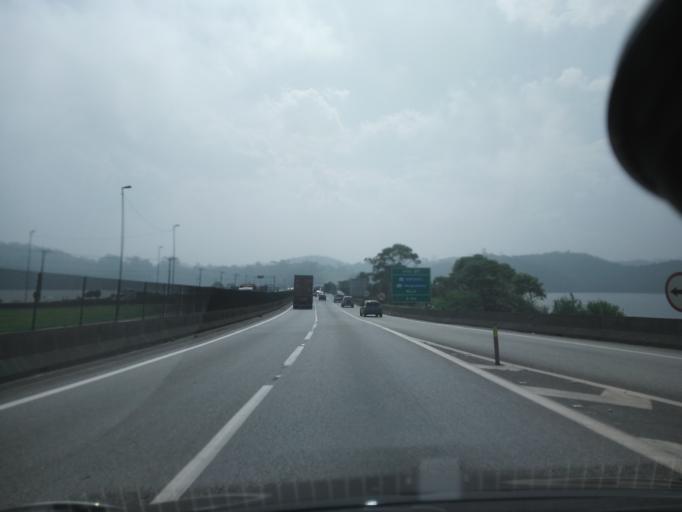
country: BR
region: Sao Paulo
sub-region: Sao Bernardo Do Campo
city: Sao Bernardo do Campo
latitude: -23.7755
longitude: -46.5291
